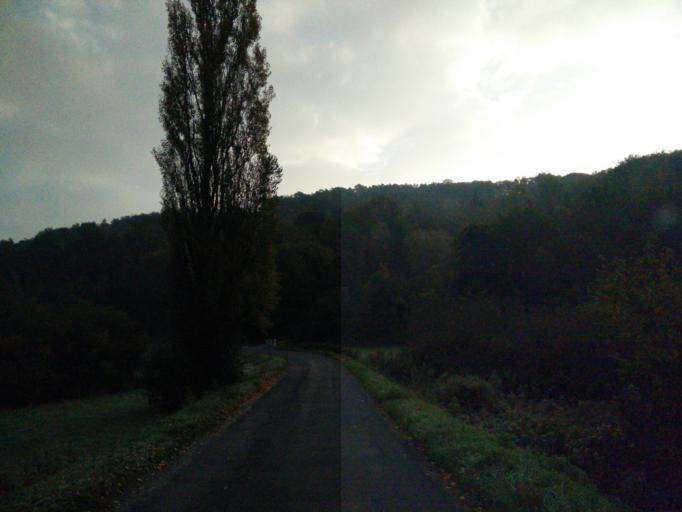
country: FR
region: Aquitaine
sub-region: Departement de la Dordogne
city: Rouffignac-Saint-Cernin-de-Reilhac
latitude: 44.9947
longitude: 0.9458
